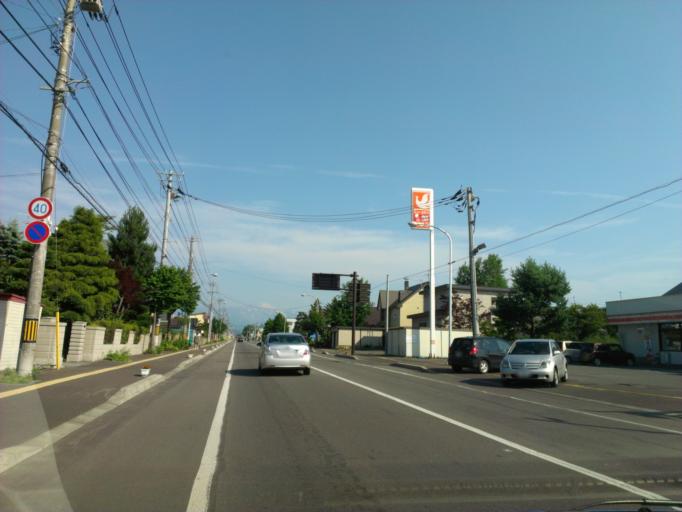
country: JP
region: Hokkaido
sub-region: Asahikawa-shi
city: Asahikawa
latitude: 43.5908
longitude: 142.4719
